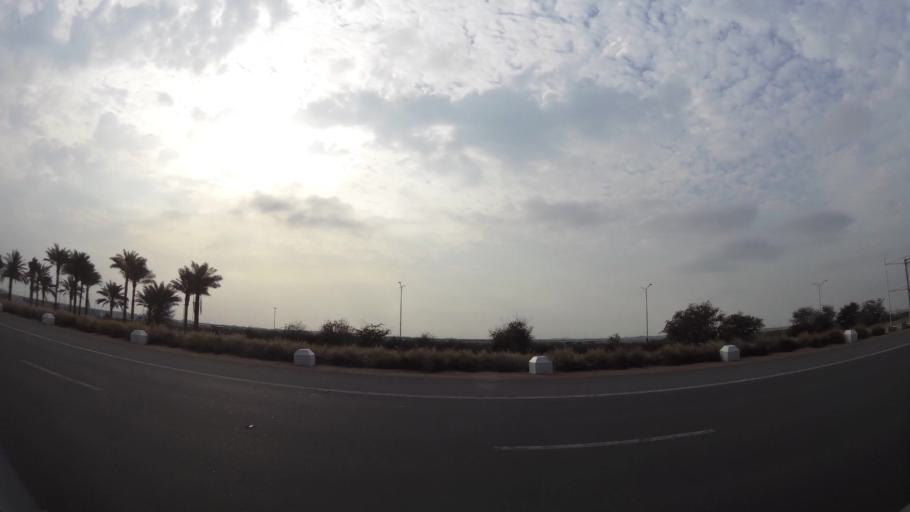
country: AE
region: Abu Dhabi
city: Abu Dhabi
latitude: 24.5446
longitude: 54.4479
